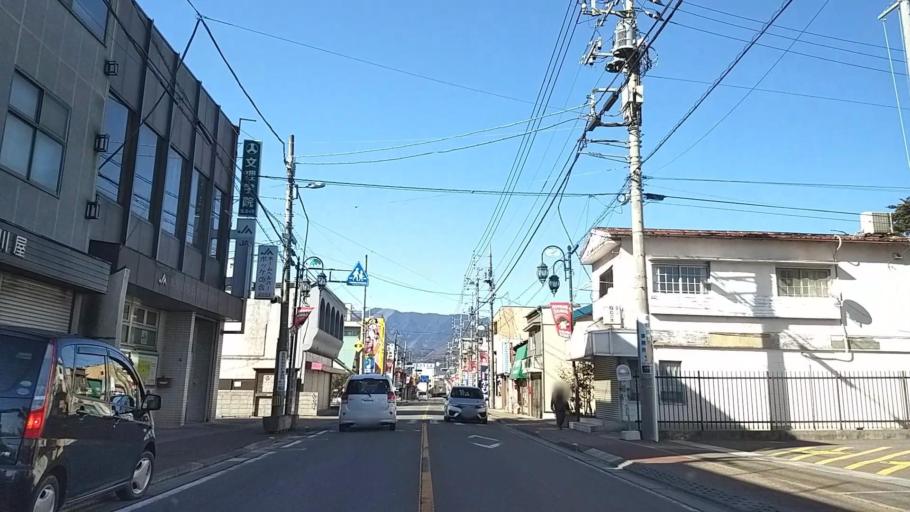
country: JP
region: Yamanashi
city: Uenohara
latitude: 35.6280
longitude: 139.1132
